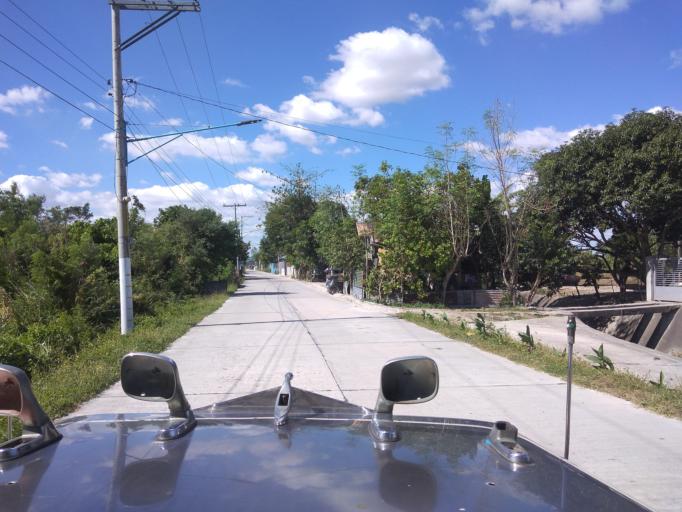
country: PH
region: Central Luzon
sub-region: Province of Pampanga
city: Bacolor
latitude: 15.0059
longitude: 120.6478
